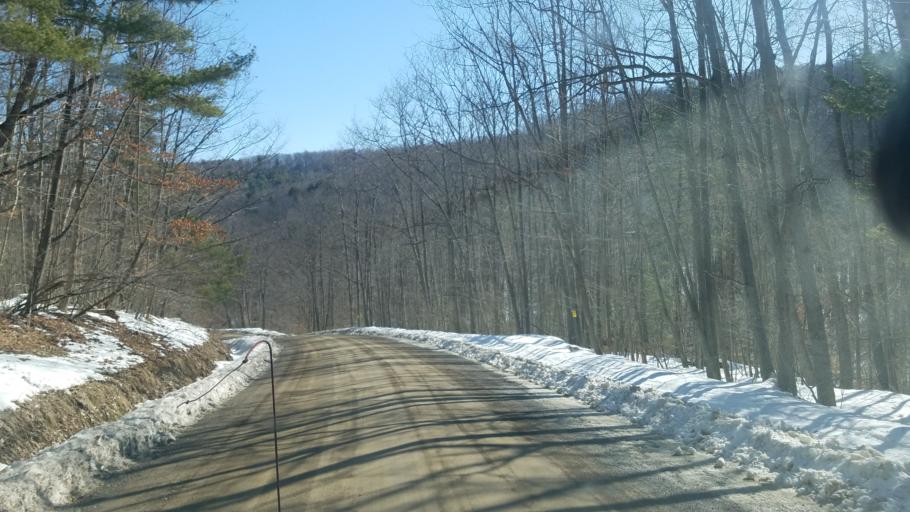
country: US
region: New York
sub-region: Allegany County
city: Alfred
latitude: 42.2466
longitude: -77.7243
